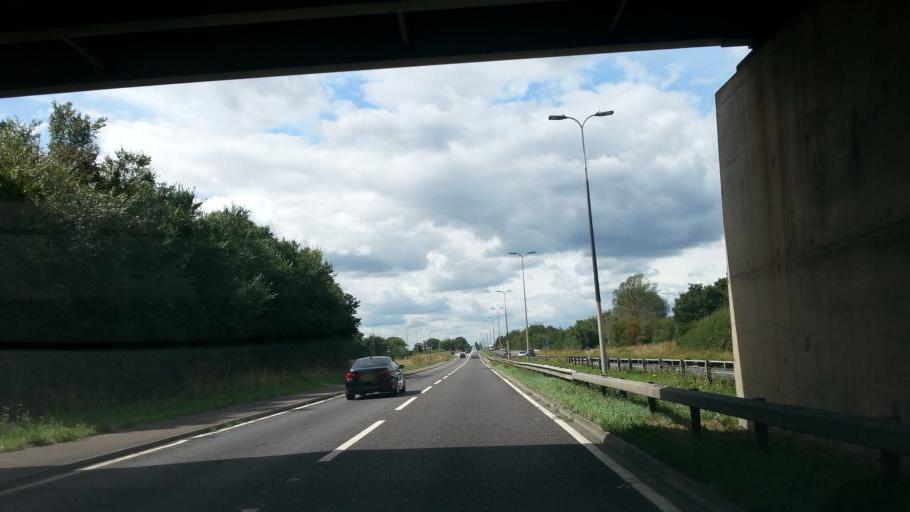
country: GB
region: England
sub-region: Essex
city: Billericay
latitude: 51.5836
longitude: 0.3918
